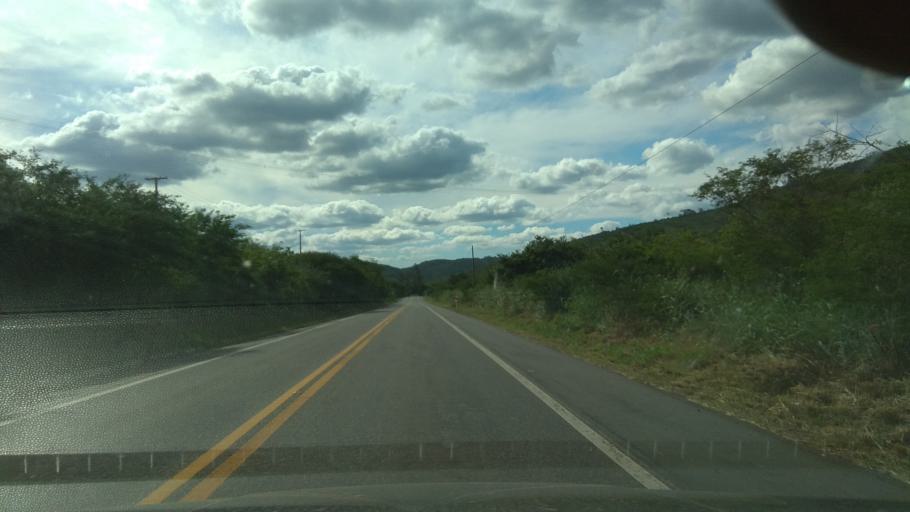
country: BR
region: Bahia
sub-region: Jequie
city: Jequie
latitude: -13.9078
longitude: -40.0172
